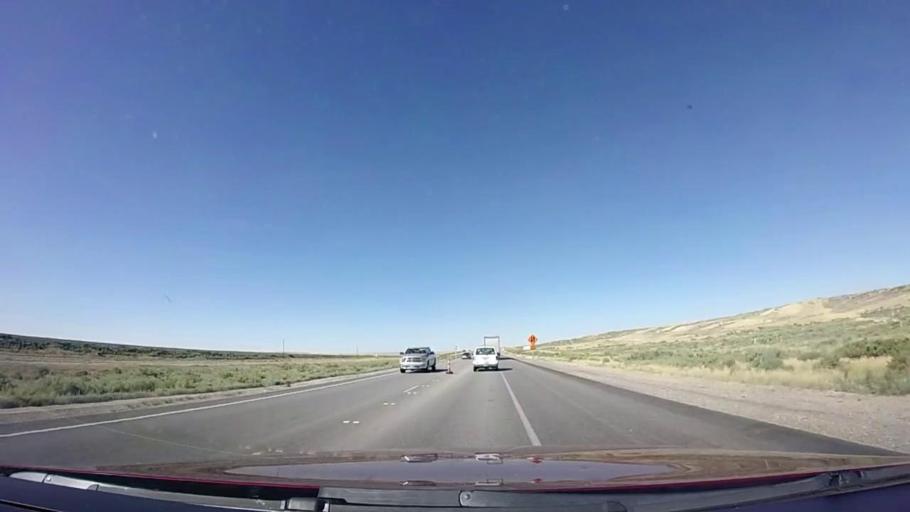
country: US
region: Wyoming
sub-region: Carbon County
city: Rawlins
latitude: 41.7016
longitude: -107.9074
